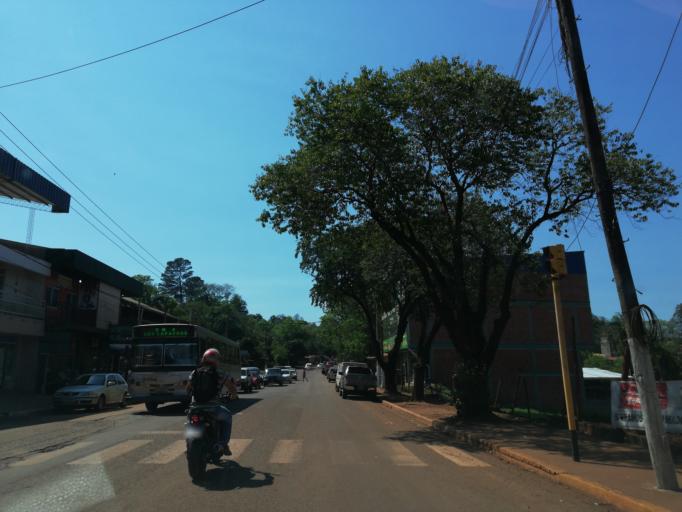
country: AR
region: Misiones
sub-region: Departamento de Eldorado
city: Eldorado
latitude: -26.4064
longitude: -54.6493
